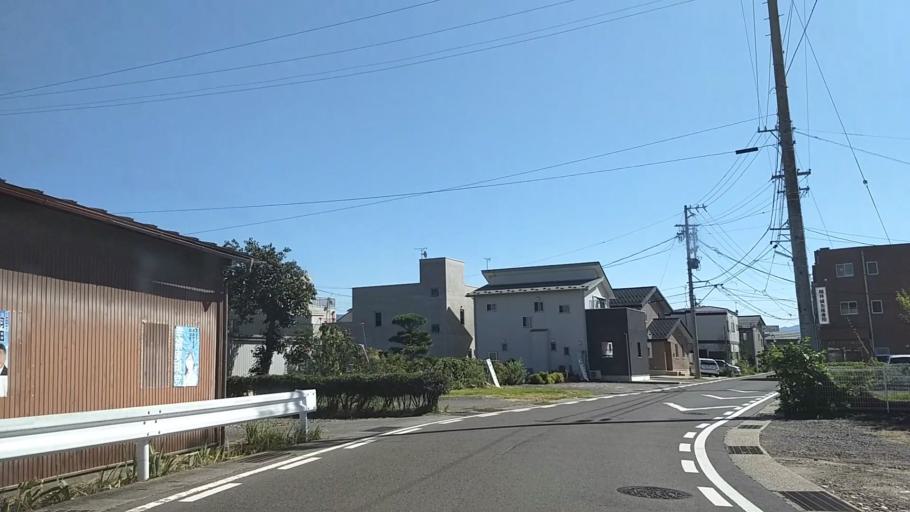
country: JP
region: Nagano
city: Nagano-shi
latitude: 36.6157
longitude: 138.1520
